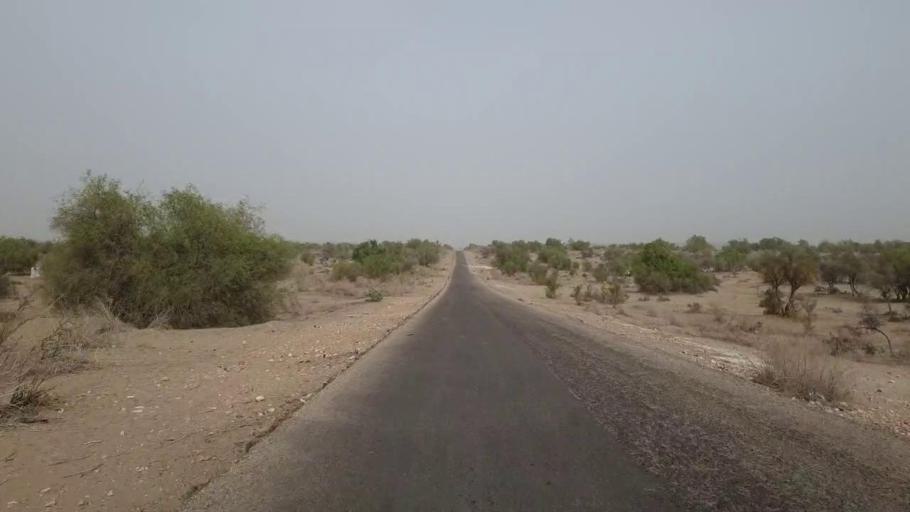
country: PK
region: Sindh
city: Islamkot
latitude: 24.5724
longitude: 70.3186
